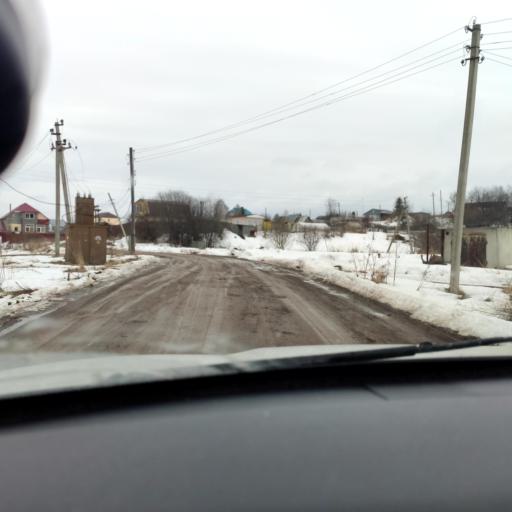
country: RU
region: Perm
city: Lobanovo
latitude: 57.8526
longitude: 56.3423
